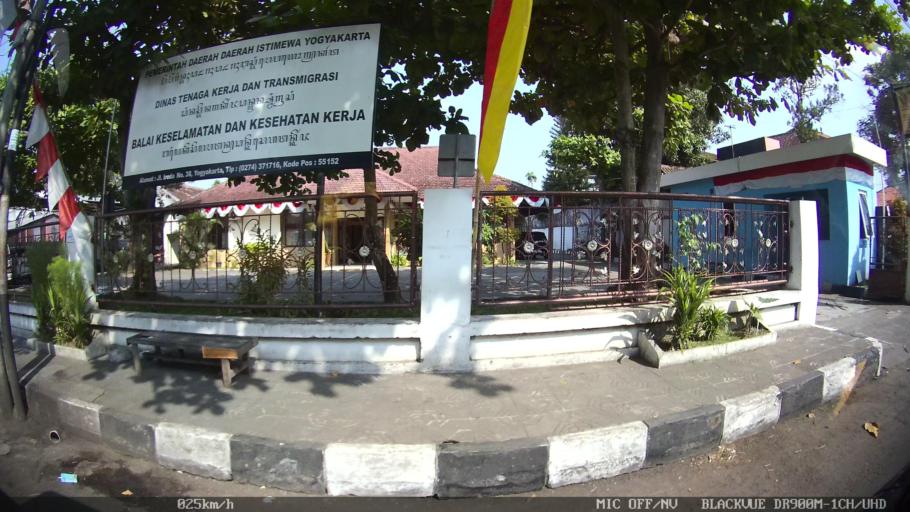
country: ID
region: Daerah Istimewa Yogyakarta
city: Yogyakarta
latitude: -7.8119
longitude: 110.3718
